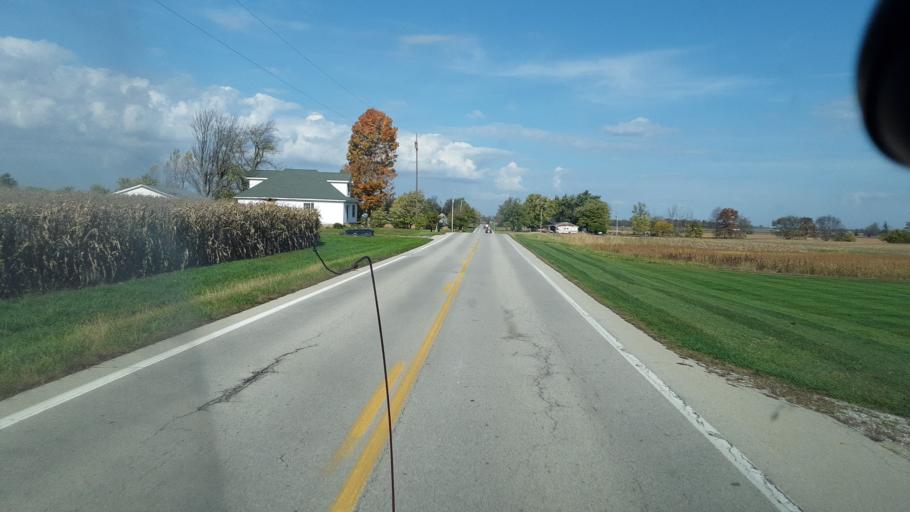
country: US
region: Ohio
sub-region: Clinton County
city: Sabina
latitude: 39.5428
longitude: -83.7098
